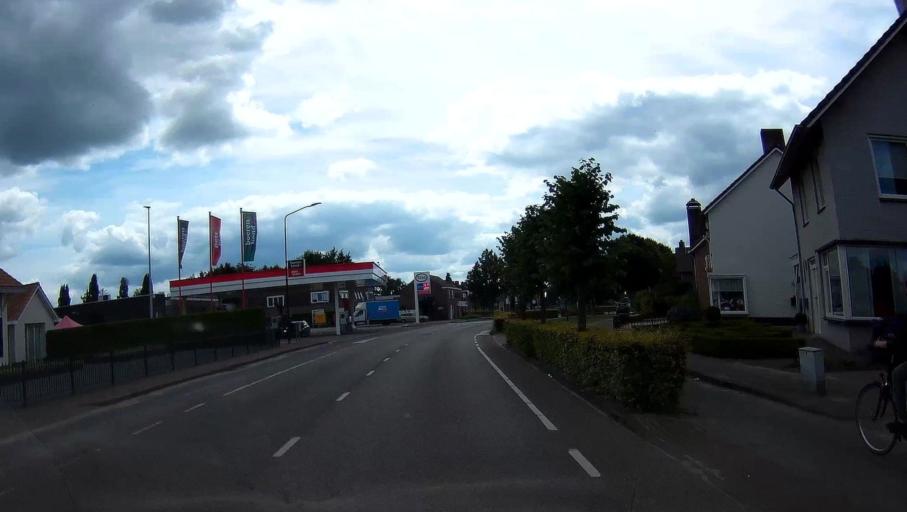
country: NL
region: North Brabant
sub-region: Gemeente Hilvarenbeek
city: Hilvarenbeek
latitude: 51.4928
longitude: 5.1353
